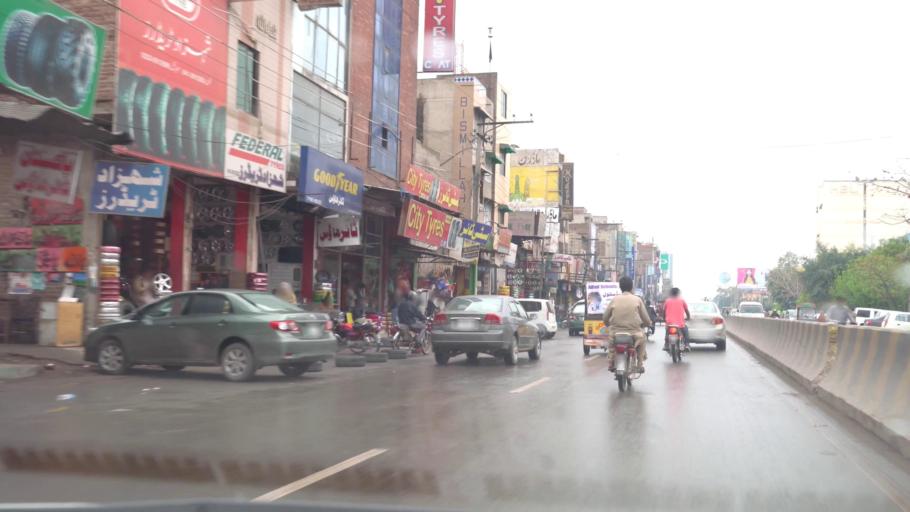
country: PK
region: Punjab
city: Faisalabad
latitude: 31.4171
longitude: 73.0878
